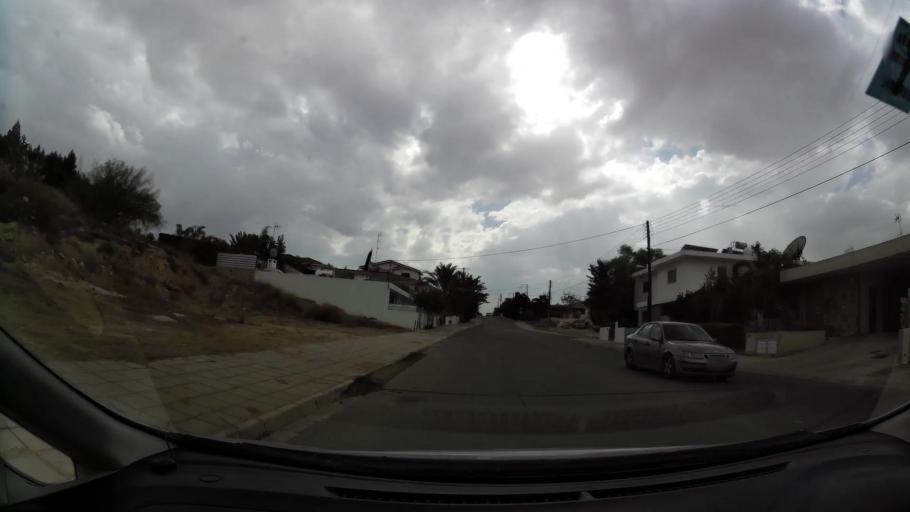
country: CY
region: Lefkosia
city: Geri
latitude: 35.1183
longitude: 33.3850
